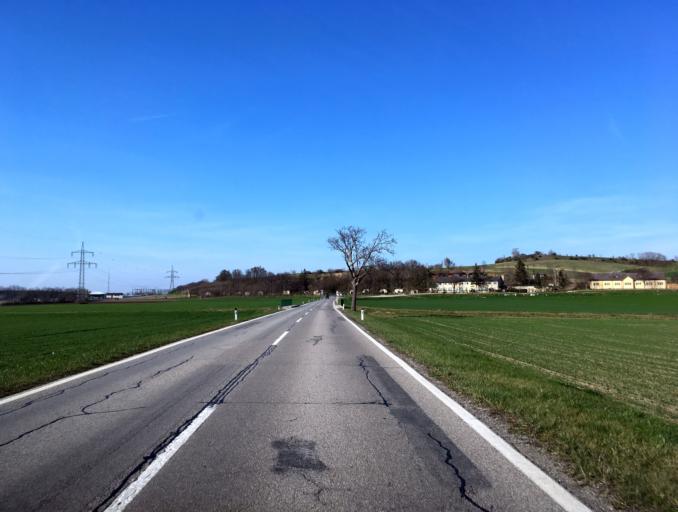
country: AT
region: Lower Austria
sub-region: Politischer Bezirk Bruck an der Leitha
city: Enzersdorf an der Fischa
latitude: 48.0587
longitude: 16.6170
